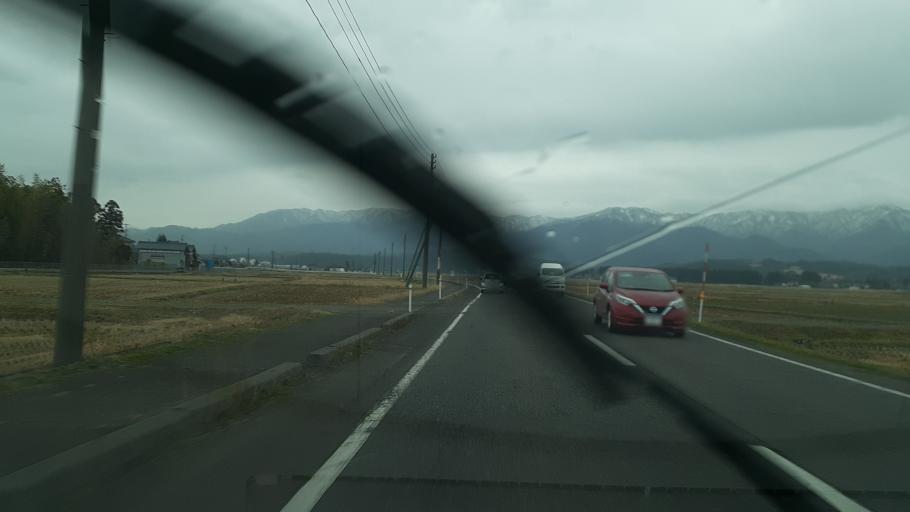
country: JP
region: Niigata
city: Suibara
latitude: 37.8328
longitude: 139.2462
